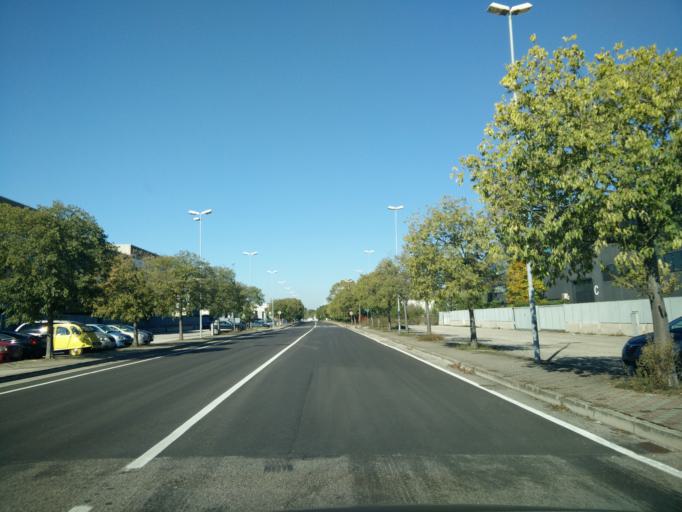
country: IT
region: Veneto
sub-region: Provincia di Venezia
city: Mestre
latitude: 45.4584
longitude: 12.2173
